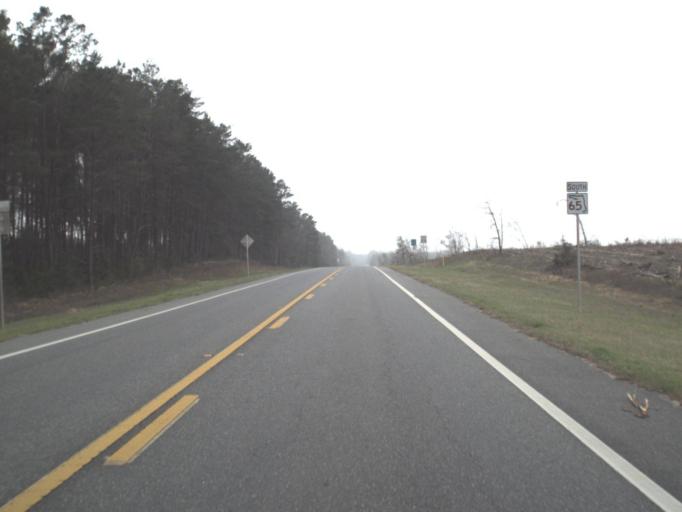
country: US
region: Florida
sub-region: Gadsden County
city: Gretna
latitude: 30.4598
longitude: -84.7422
